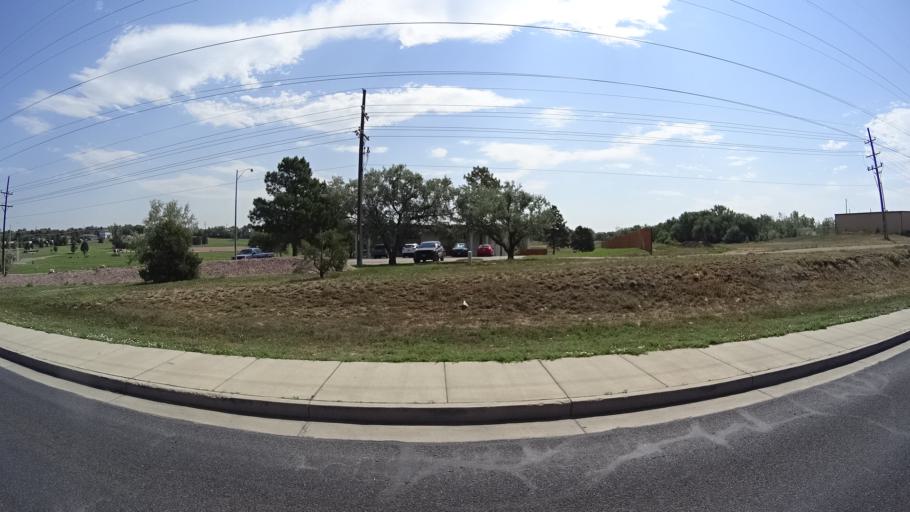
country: US
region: Colorado
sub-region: El Paso County
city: Stratmoor
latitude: 38.8226
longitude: -104.7574
